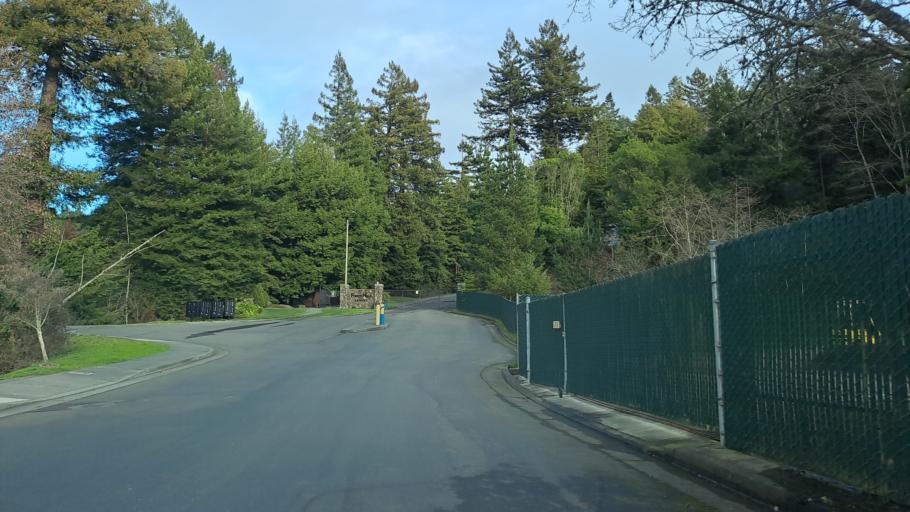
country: US
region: California
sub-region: Humboldt County
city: Fortuna
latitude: 40.5770
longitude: -124.1279
